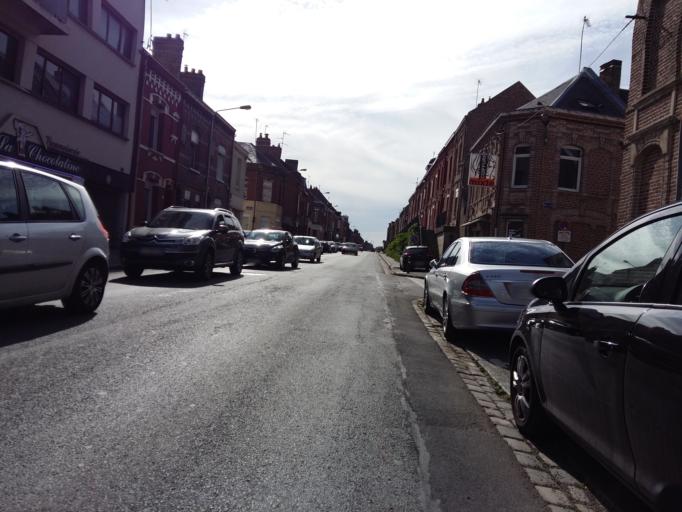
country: FR
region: Picardie
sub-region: Departement de la Somme
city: Rivery
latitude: 49.9032
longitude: 2.3152
